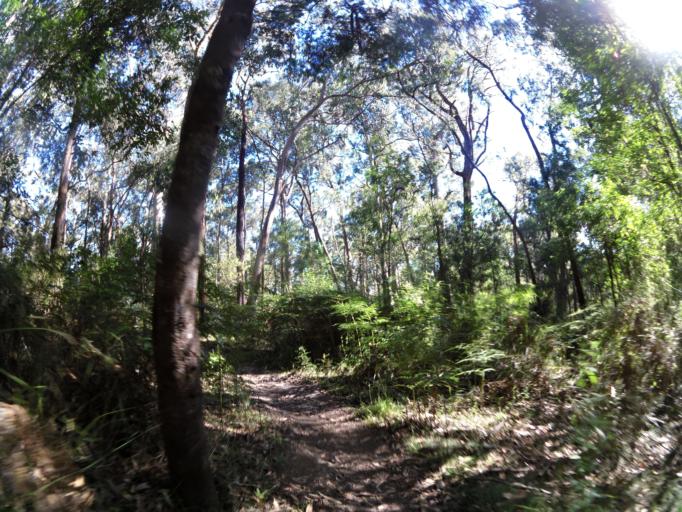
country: AU
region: Victoria
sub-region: Colac-Otway
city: Apollo Bay
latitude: -38.5474
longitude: 143.7351
